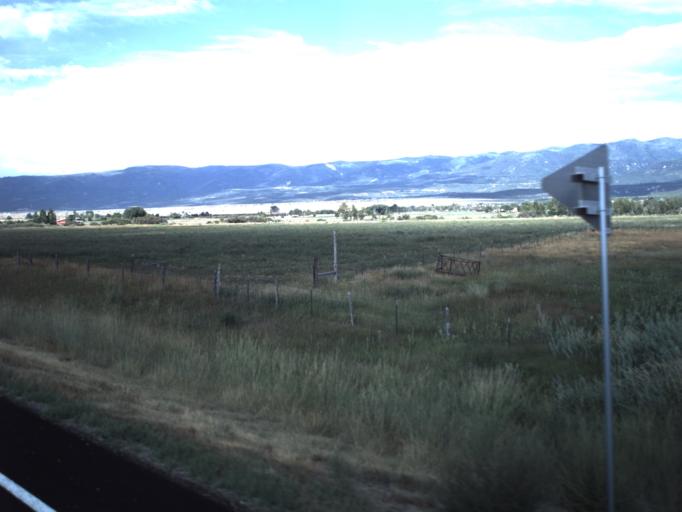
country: US
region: Utah
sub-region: Sanpete County
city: Moroni
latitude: 39.4831
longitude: -111.5200
